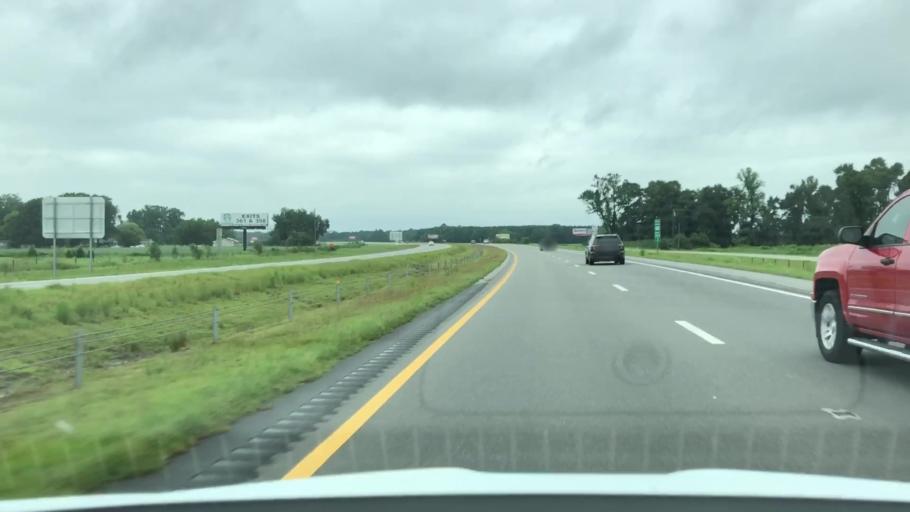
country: US
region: North Carolina
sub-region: Wayne County
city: Elroy
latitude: 35.3880
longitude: -77.8654
